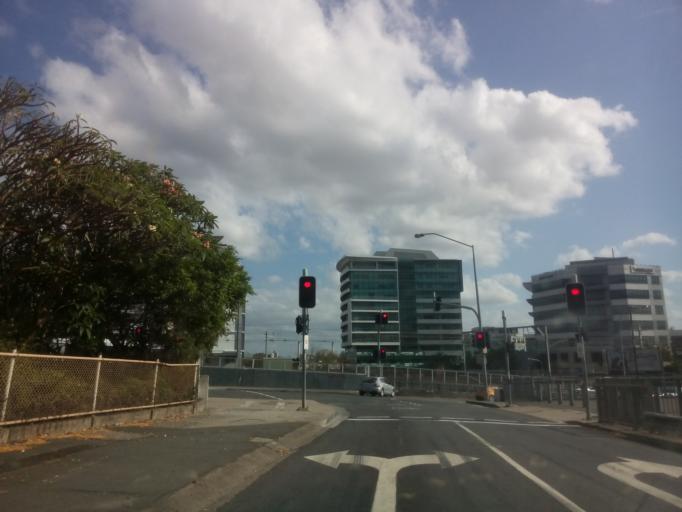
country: AU
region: Queensland
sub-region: Brisbane
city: Milton
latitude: -27.4663
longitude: 153.0107
